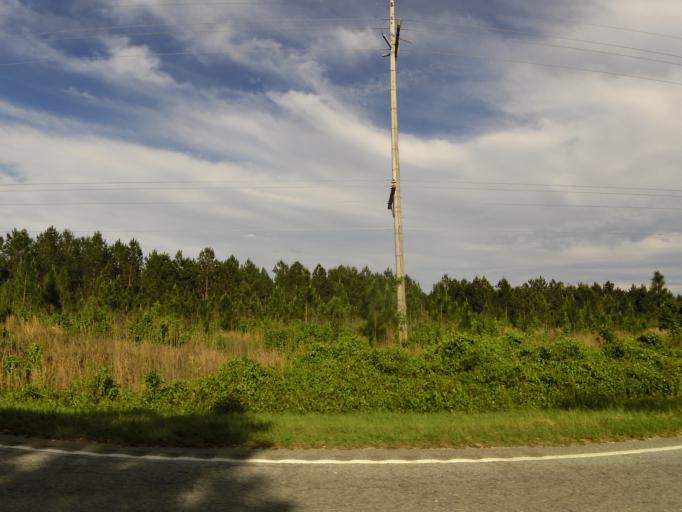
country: US
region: South Carolina
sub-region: Allendale County
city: Fairfax
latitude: 32.8825
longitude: -81.2382
